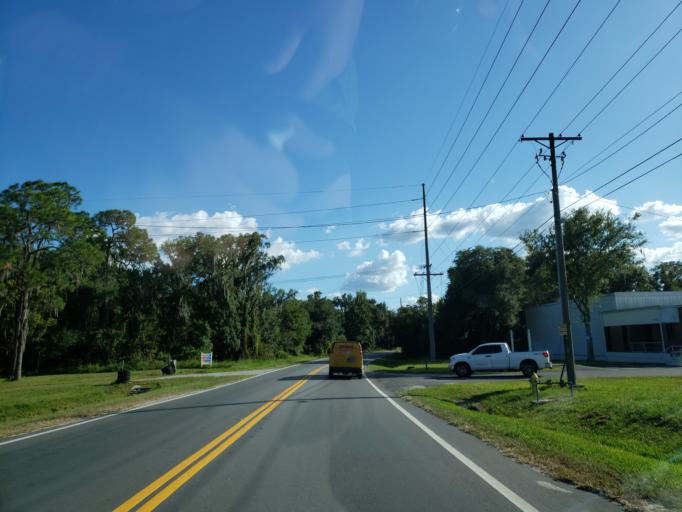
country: US
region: Florida
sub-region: Hillsborough County
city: Plant City
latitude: 28.0041
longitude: -82.1463
